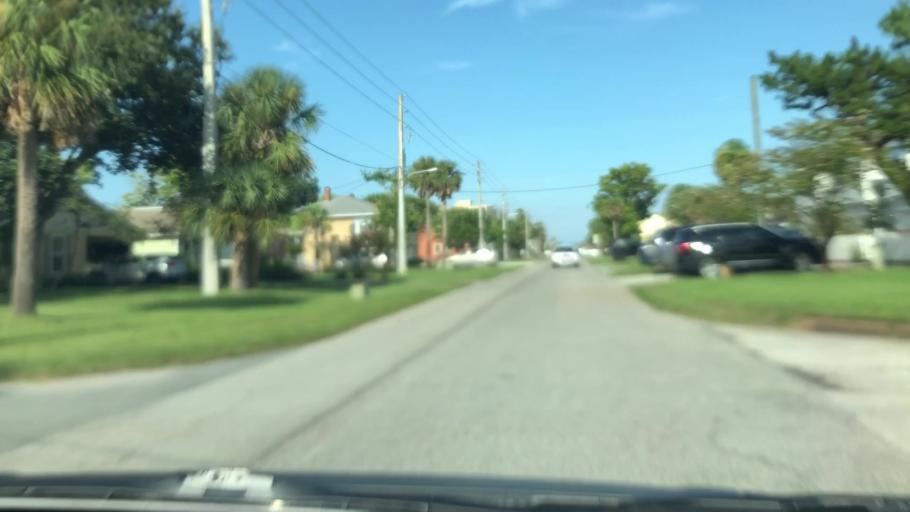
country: US
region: Florida
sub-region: Duval County
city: Jacksonville Beach
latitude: 30.2903
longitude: -81.3968
